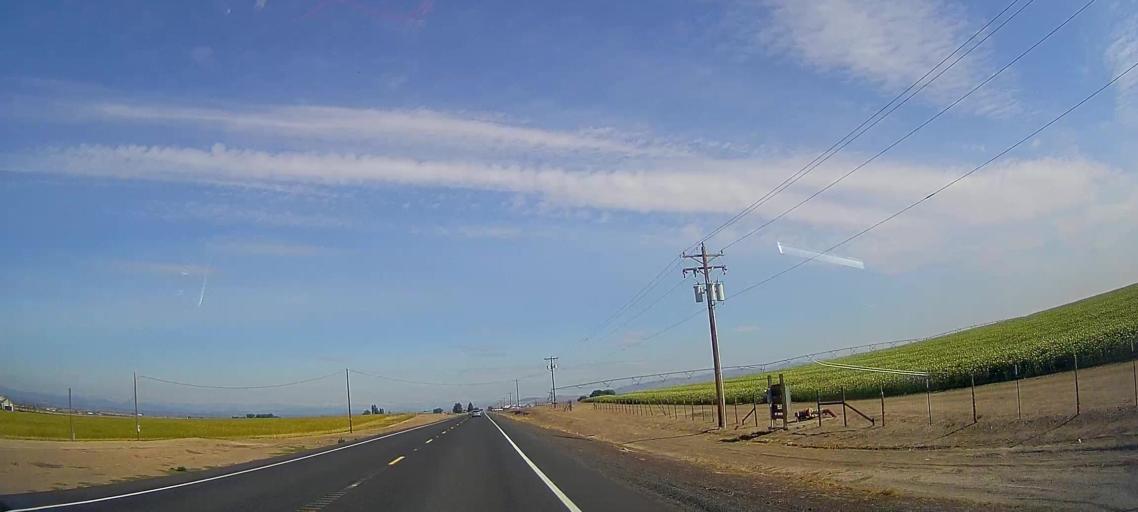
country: US
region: Oregon
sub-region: Jefferson County
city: Madras
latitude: 44.6833
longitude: -121.1493
